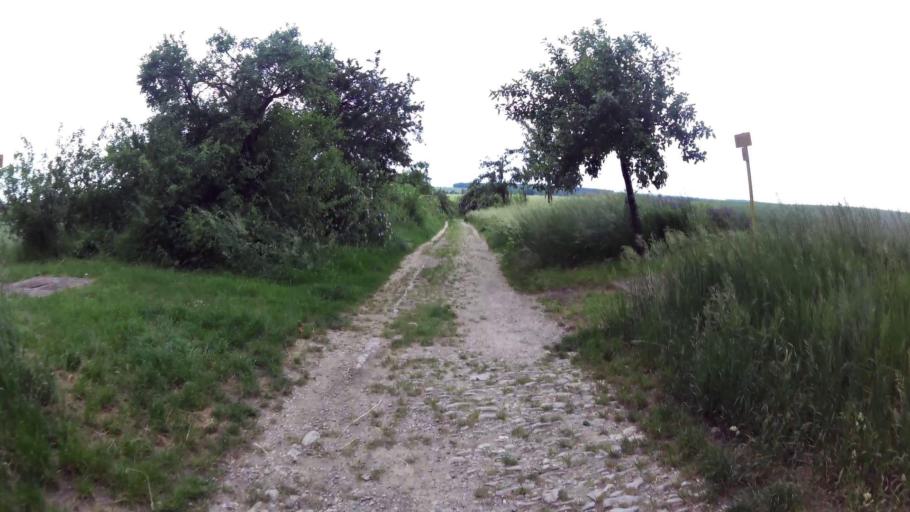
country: DE
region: Thuringia
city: Weimar
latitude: 50.9702
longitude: 11.3104
